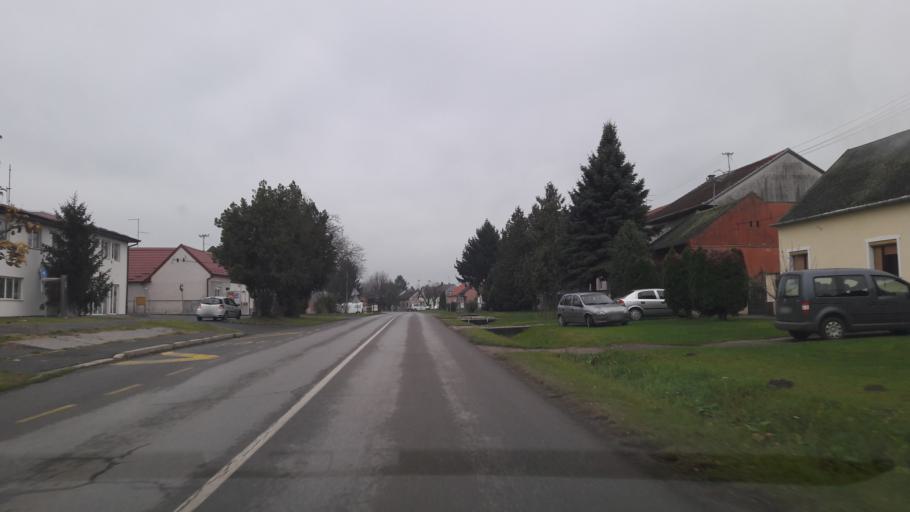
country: HR
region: Osjecko-Baranjska
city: Josipovac
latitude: 45.5773
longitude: 18.5874
